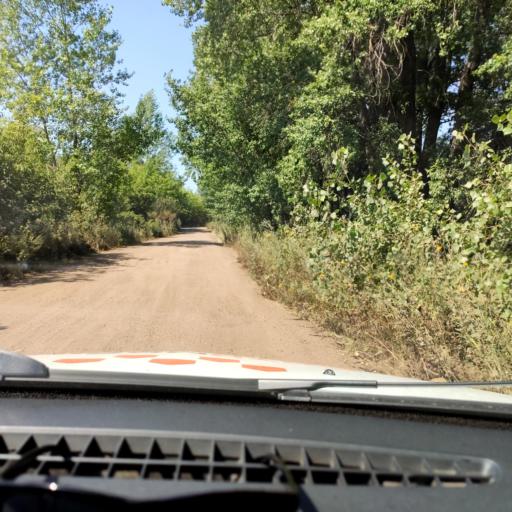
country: RU
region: Bashkortostan
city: Ufa
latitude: 54.8162
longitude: 55.9873
